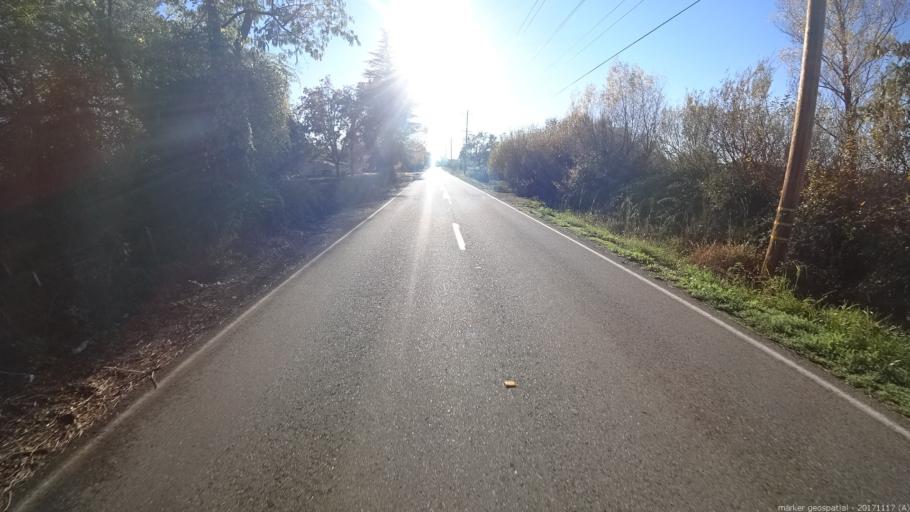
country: US
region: California
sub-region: Shasta County
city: Cottonwood
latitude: 40.4073
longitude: -122.2273
